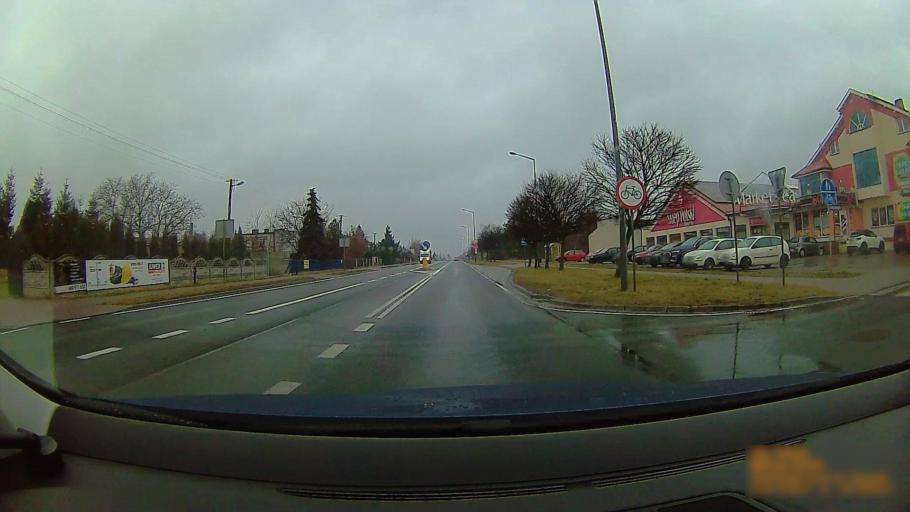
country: PL
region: Greater Poland Voivodeship
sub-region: Konin
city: Konin
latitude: 52.1772
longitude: 18.2713
